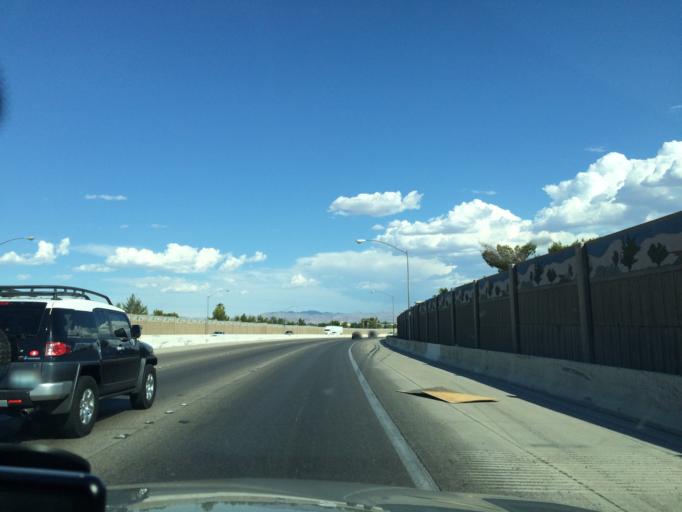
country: US
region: Nevada
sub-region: Clark County
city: North Las Vegas
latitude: 36.1656
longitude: -115.0958
